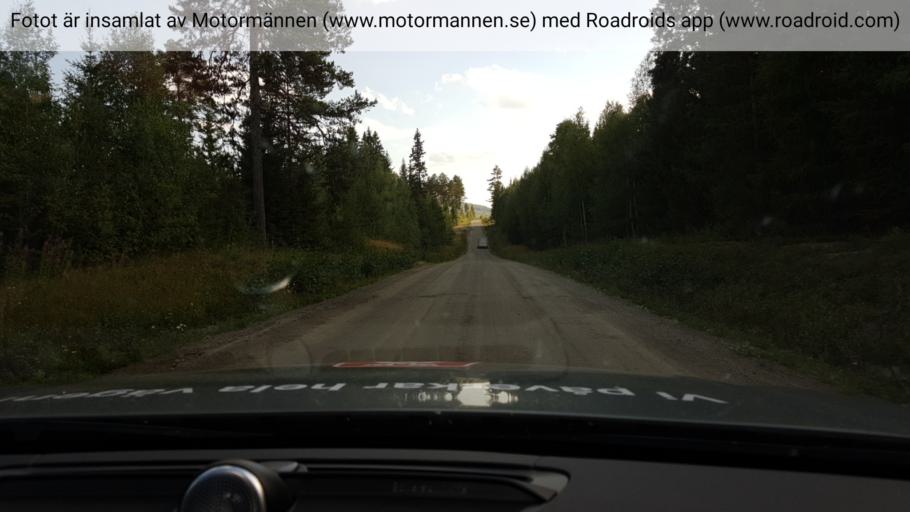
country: SE
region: Vaesternorrland
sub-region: Solleftea Kommun
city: As
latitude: 63.7899
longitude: 16.3919
